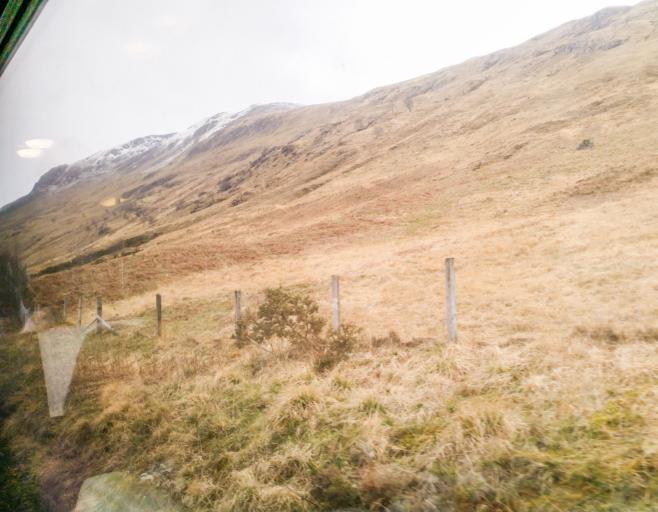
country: GB
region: Scotland
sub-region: Highland
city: Spean Bridge
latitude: 56.8153
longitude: -4.7150
